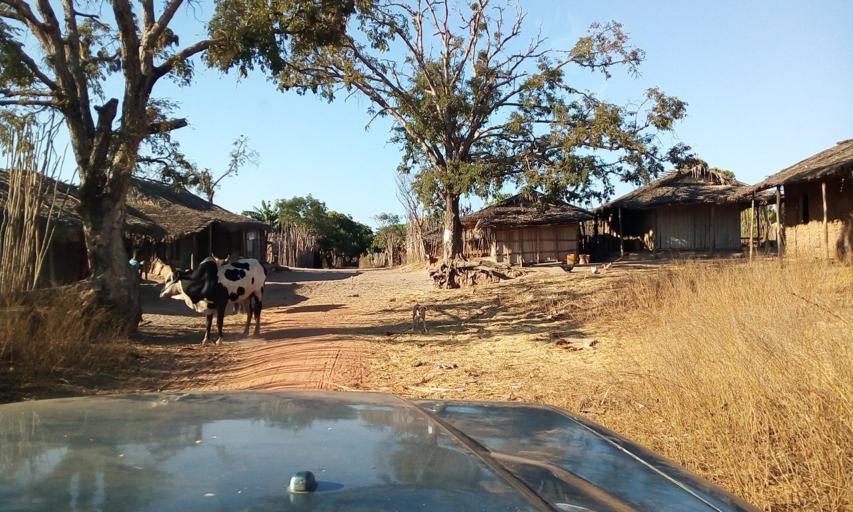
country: MG
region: Boeny
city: Sitampiky
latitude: -16.1491
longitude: 45.3445
